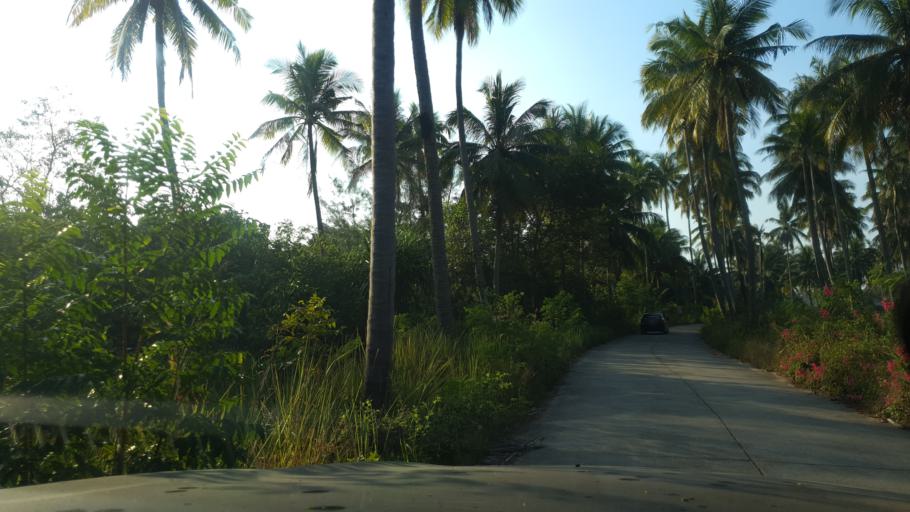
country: TH
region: Prachuap Khiri Khan
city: Bang Saphan
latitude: 11.2997
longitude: 99.5498
